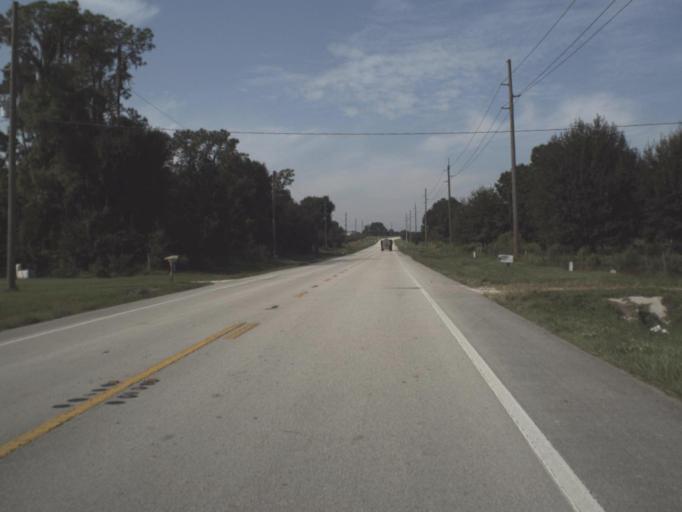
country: US
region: Florida
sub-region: Hardee County
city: Wauchula
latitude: 27.5613
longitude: -81.6628
